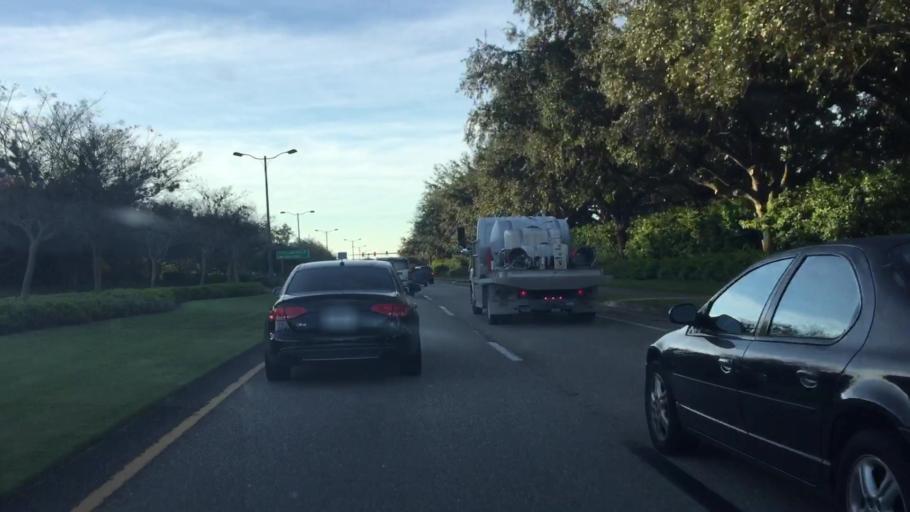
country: US
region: Florida
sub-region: Lee County
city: Three Oaks
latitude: 26.4724
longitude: -81.7865
